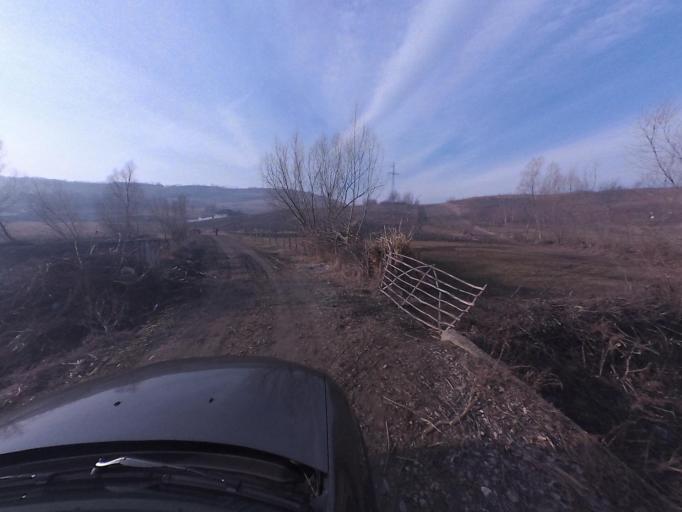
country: RO
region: Vaslui
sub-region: Comuna Solesti
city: Solesti
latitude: 46.8144
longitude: 27.7632
